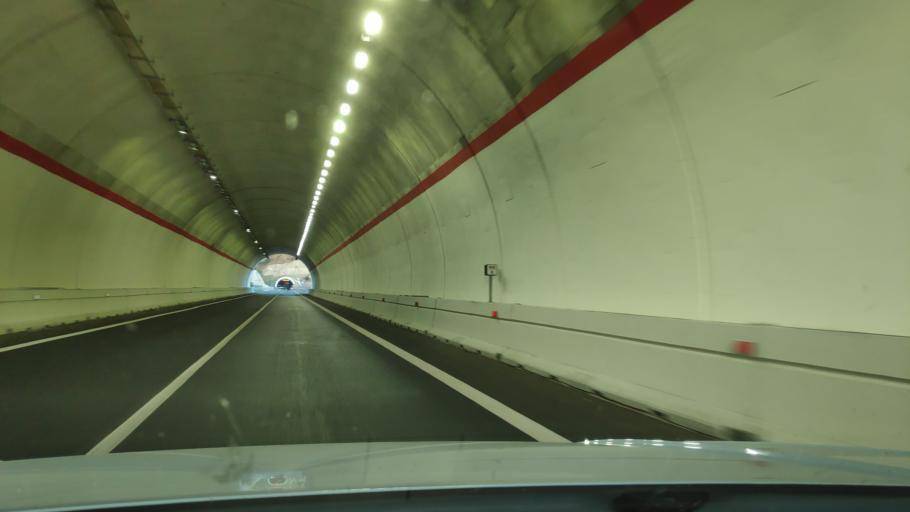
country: IT
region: Calabria
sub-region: Provincia di Reggio Calabria
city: Palizzi Marina
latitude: 37.9228
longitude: 15.9806
